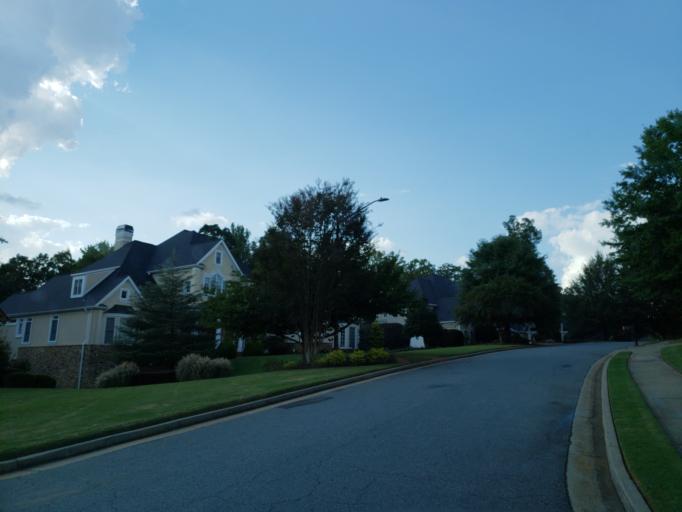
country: US
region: Georgia
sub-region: Cherokee County
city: Woodstock
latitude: 34.0572
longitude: -84.4446
